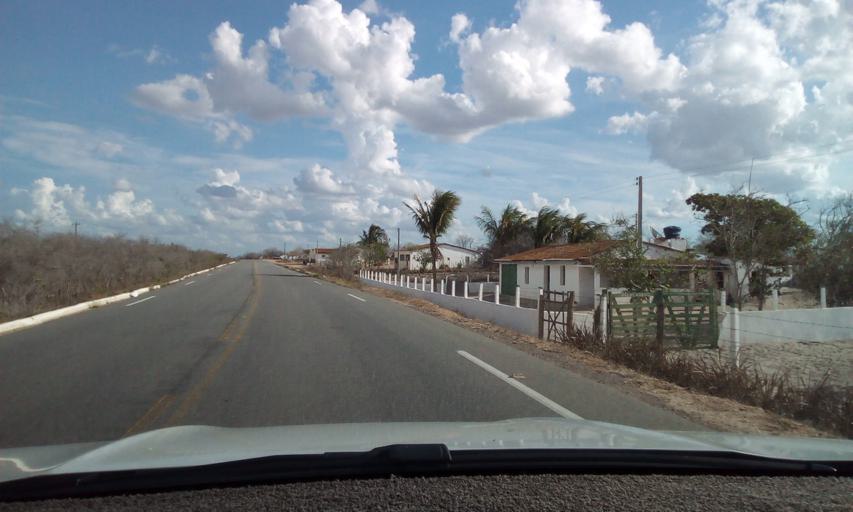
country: BR
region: Paraiba
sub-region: Soledade
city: Soledade
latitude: -6.8923
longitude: -36.3976
